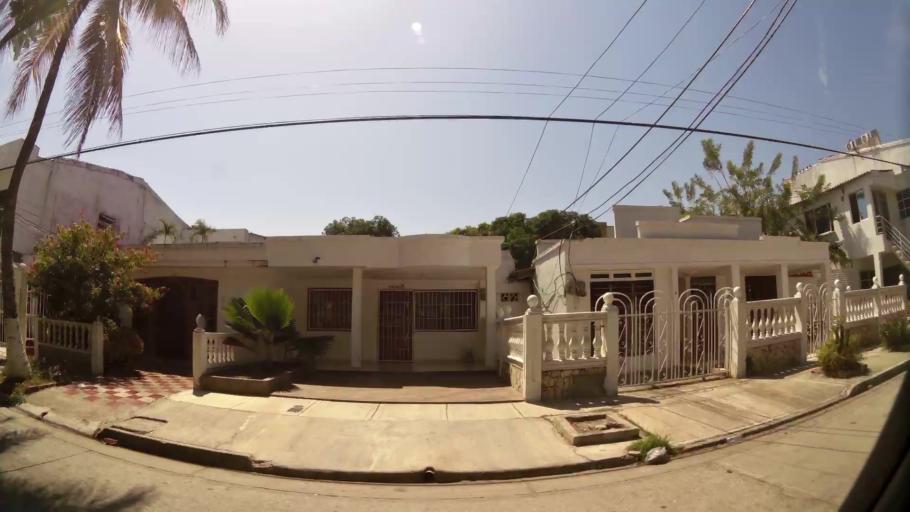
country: CO
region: Bolivar
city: Cartagena
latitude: 10.4493
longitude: -75.5167
